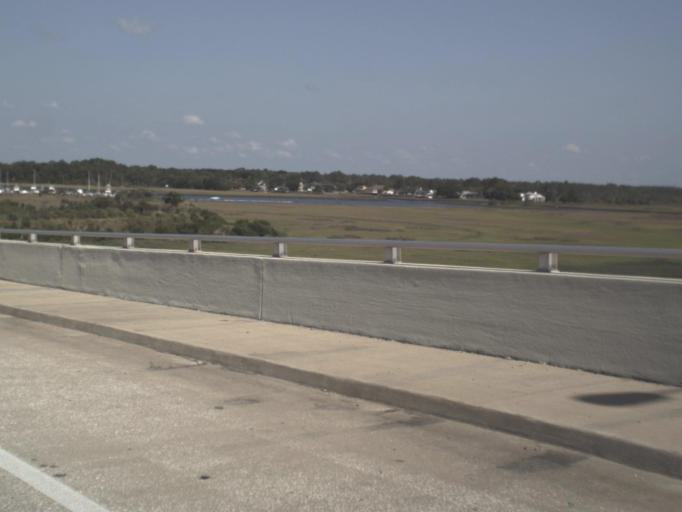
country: US
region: Florida
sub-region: Duval County
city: Jacksonville Beach
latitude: 30.2883
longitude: -81.4238
